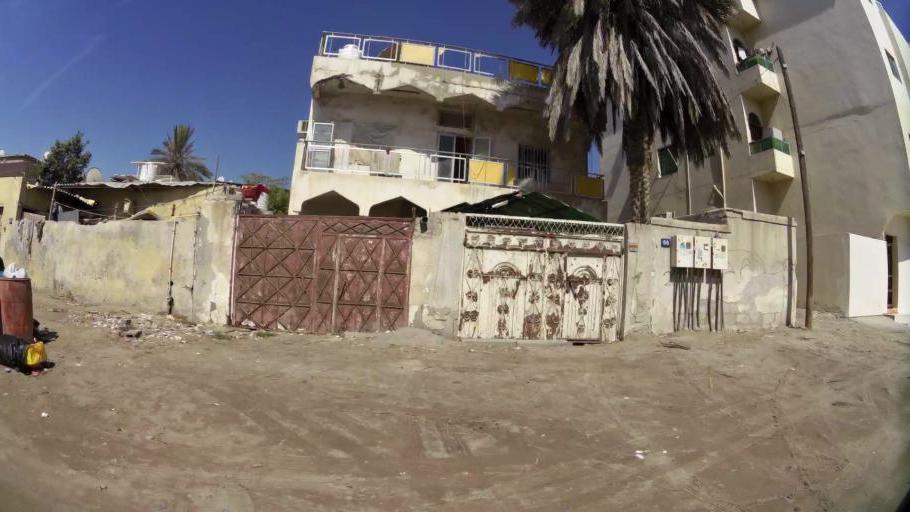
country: AE
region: Ajman
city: Ajman
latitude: 25.4102
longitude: 55.4507
